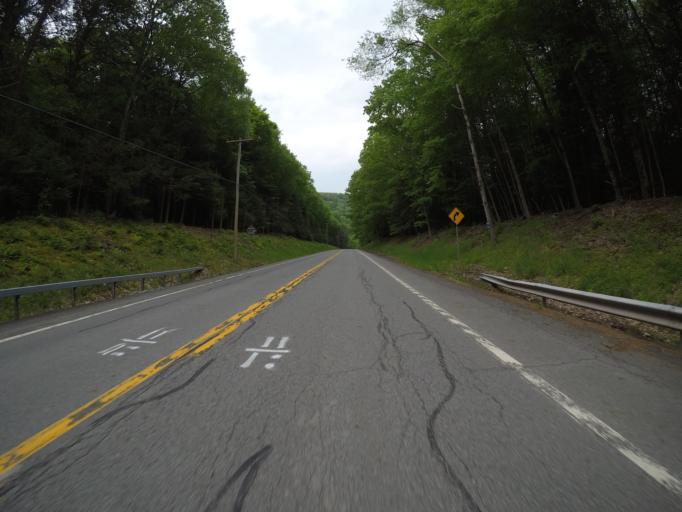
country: US
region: New York
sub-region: Sullivan County
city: Livingston Manor
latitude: 42.0731
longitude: -74.9056
